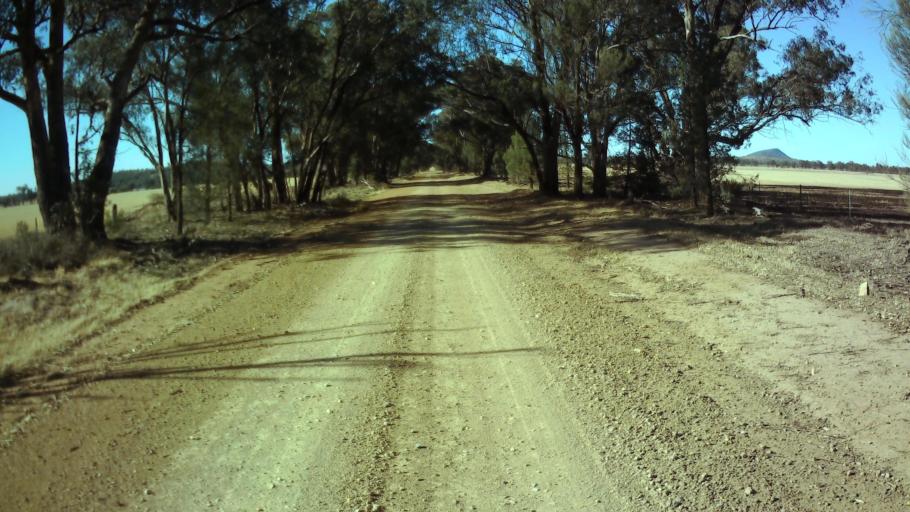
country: AU
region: New South Wales
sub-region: Weddin
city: Grenfell
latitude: -33.8170
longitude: 147.8761
